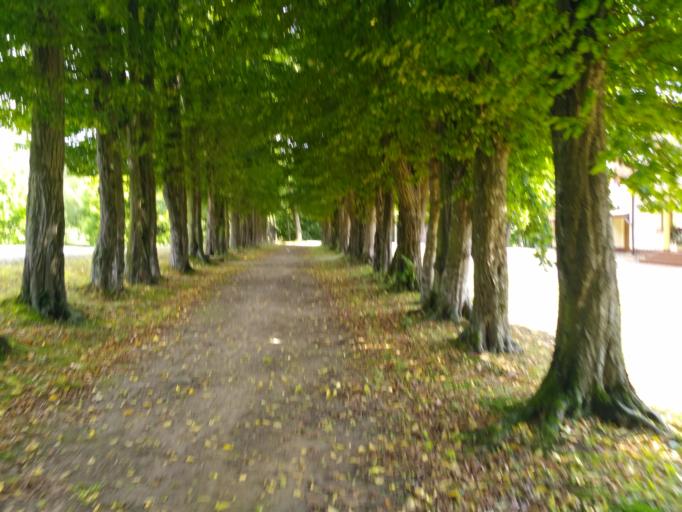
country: PL
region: Subcarpathian Voivodeship
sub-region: Powiat strzyzowski
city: Wisniowa
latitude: 49.8694
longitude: 21.6452
